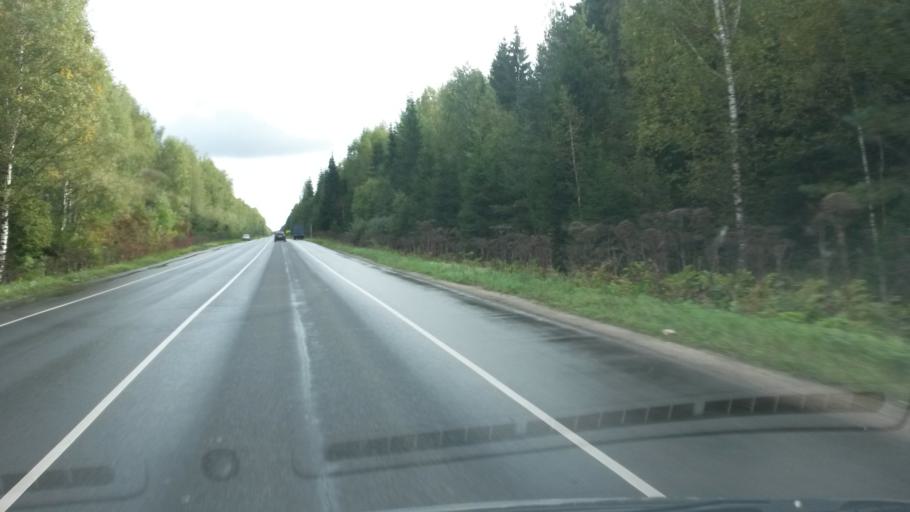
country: RU
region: Ivanovo
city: Kaminskiy
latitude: 57.0419
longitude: 41.3413
